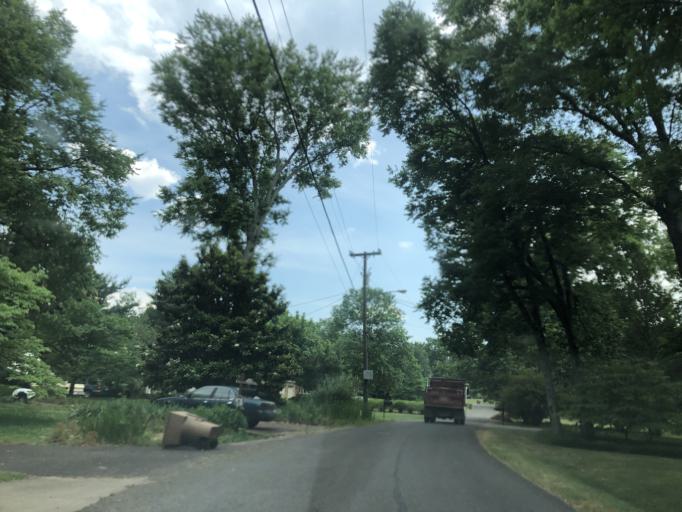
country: US
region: Tennessee
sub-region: Davidson County
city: Belle Meade
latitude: 36.1222
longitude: -86.8183
